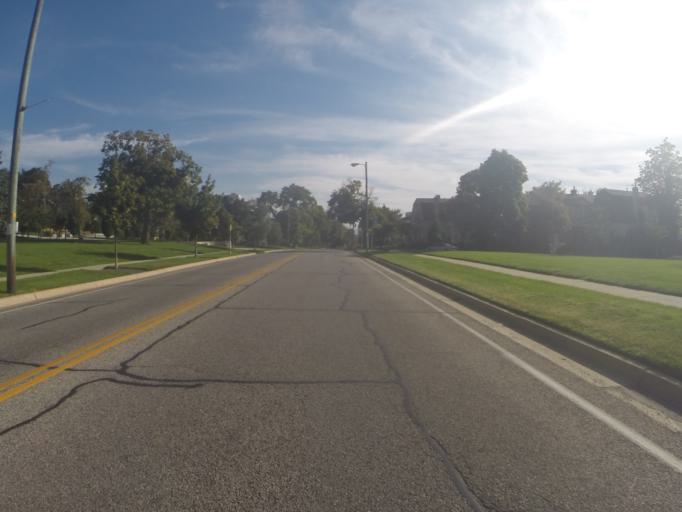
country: US
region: Utah
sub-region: Salt Lake County
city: Salt Lake City
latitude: 40.7781
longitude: -111.8905
